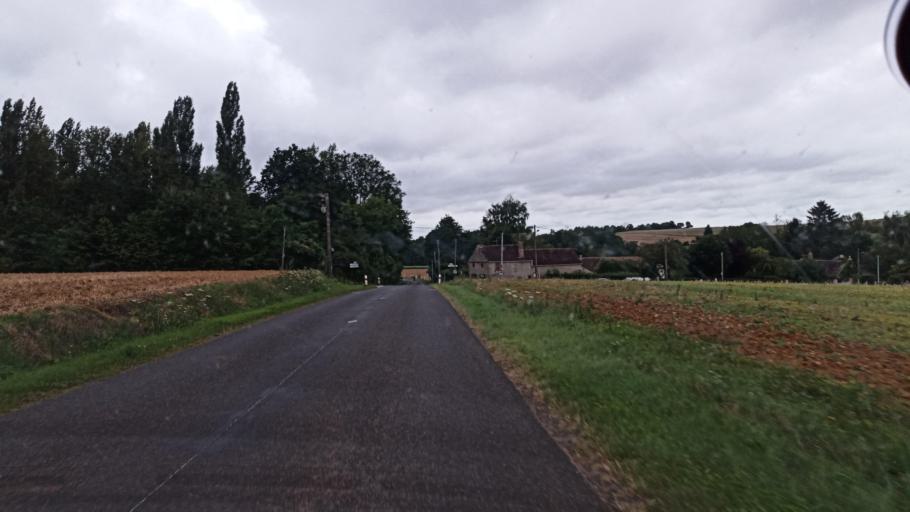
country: FR
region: Bourgogne
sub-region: Departement de l'Yonne
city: Cheroy
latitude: 48.2509
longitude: 3.0297
